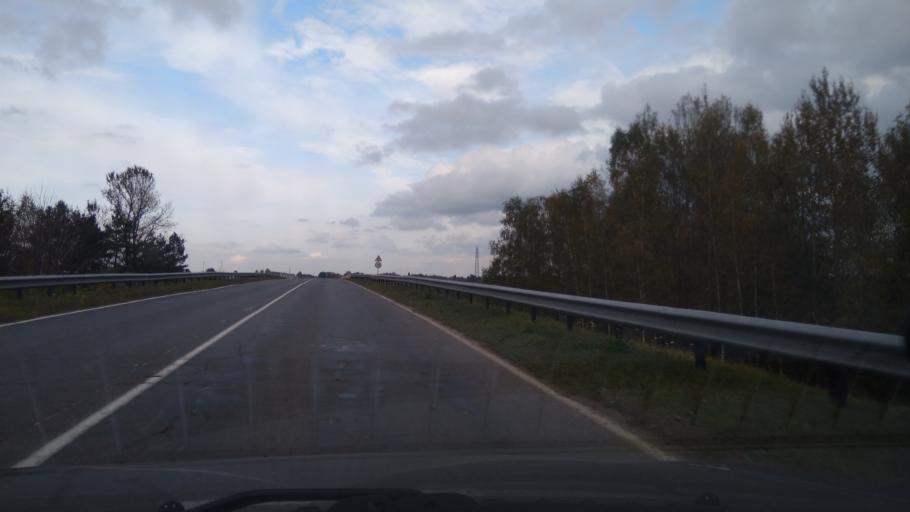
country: BY
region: Minsk
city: Dukora
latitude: 53.6588
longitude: 27.9470
